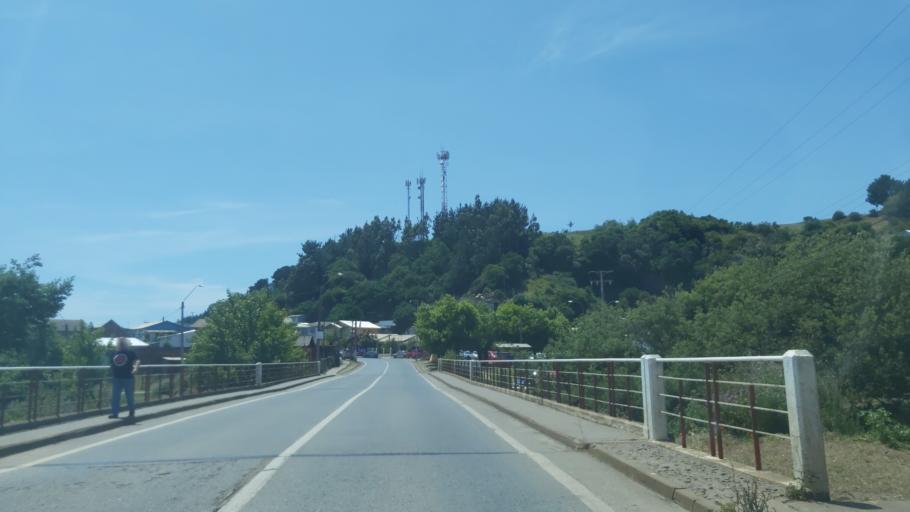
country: CL
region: Maule
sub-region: Provincia de Cauquenes
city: Cauquenes
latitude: -35.8435
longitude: -72.6314
